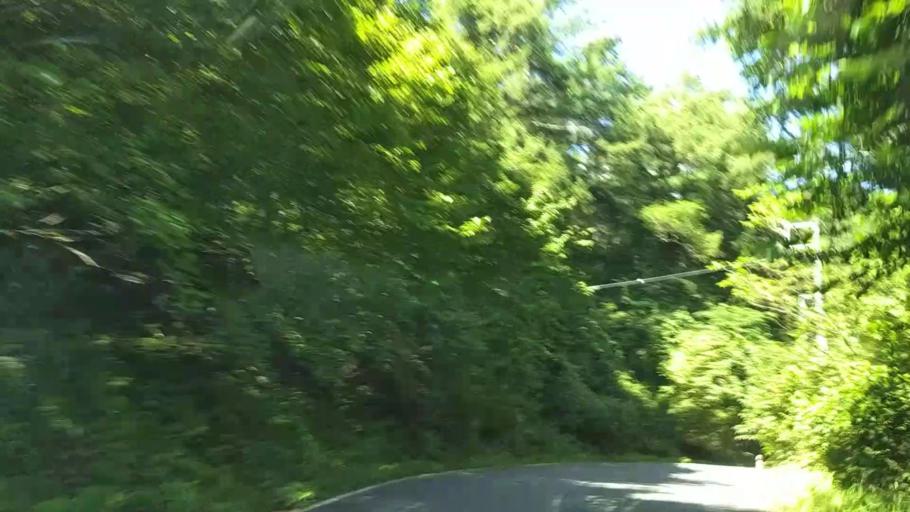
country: JP
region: Nagano
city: Matsumoto
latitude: 36.2038
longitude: 138.0928
